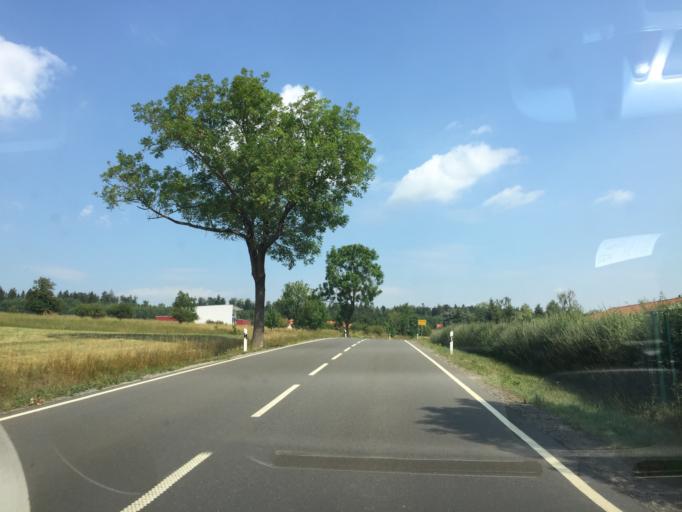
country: DE
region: Saxony-Anhalt
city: Elbingerode
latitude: 51.7660
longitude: 10.7853
